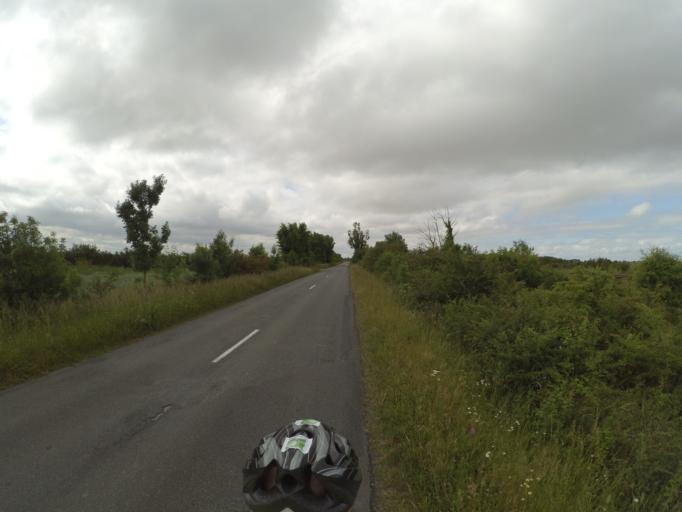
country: FR
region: Poitou-Charentes
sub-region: Departement de la Charente-Maritime
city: Yves
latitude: 46.0352
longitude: -1.0463
